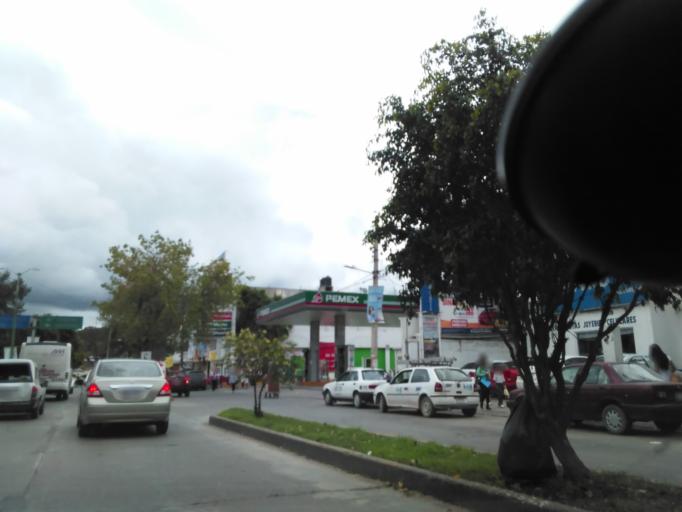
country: MX
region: Hidalgo
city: Tula de Allende
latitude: 20.0546
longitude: -99.3392
